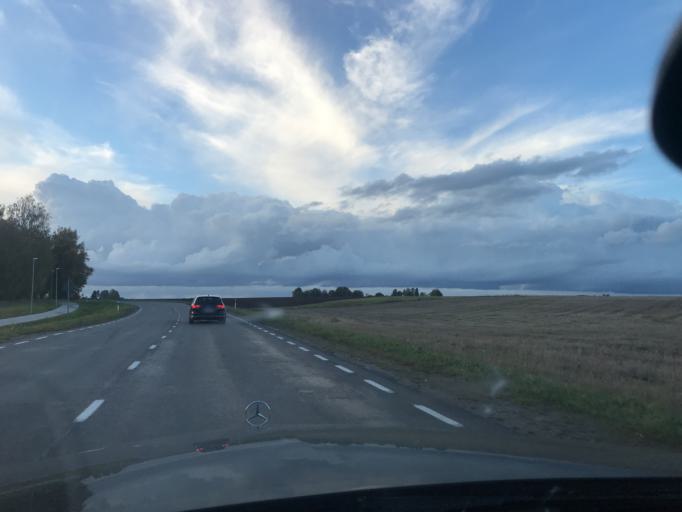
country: EE
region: Vorumaa
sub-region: Antsla vald
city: Vana-Antsla
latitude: 57.8937
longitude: 26.4988
